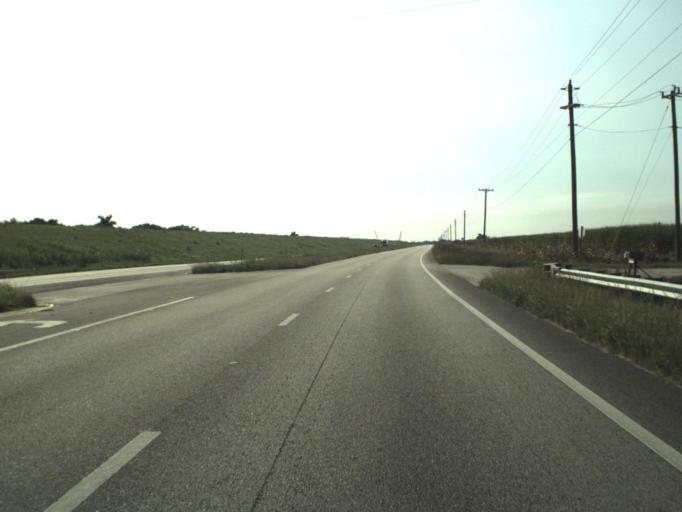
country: US
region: Florida
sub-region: Palm Beach County
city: South Bay
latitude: 26.6941
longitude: -80.7733
